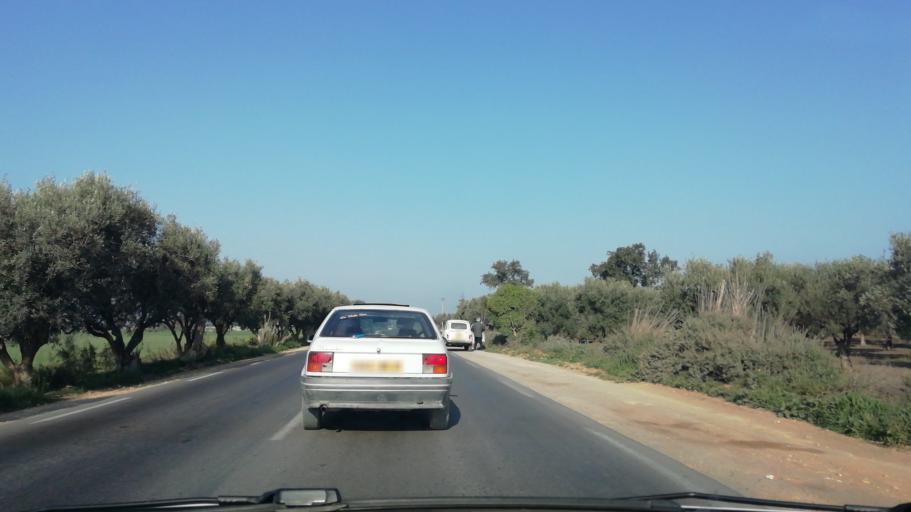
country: DZ
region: Mostaganem
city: Mostaganem
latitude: 35.7543
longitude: 0.1149
